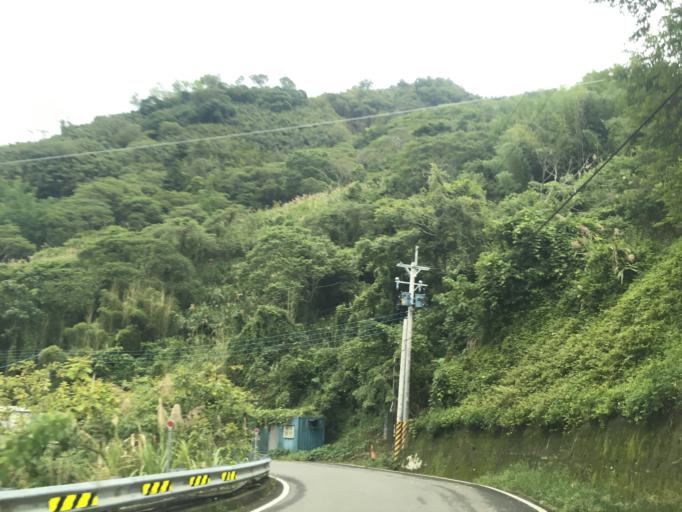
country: TW
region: Taiwan
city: Lugu
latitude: 23.5342
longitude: 120.7071
